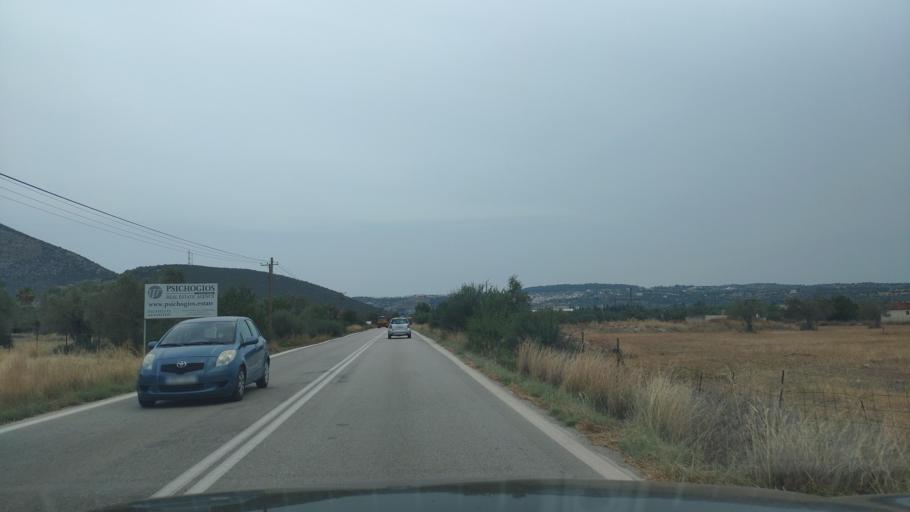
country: GR
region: Peloponnese
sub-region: Nomos Argolidos
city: Koilas
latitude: 37.4098
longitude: 23.1535
